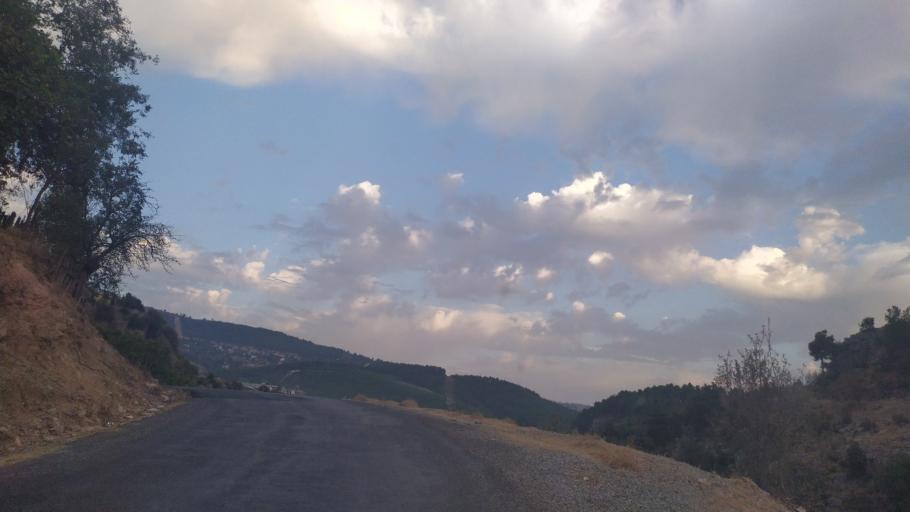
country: TR
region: Mersin
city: Camliyayla
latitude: 37.2385
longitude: 34.7159
